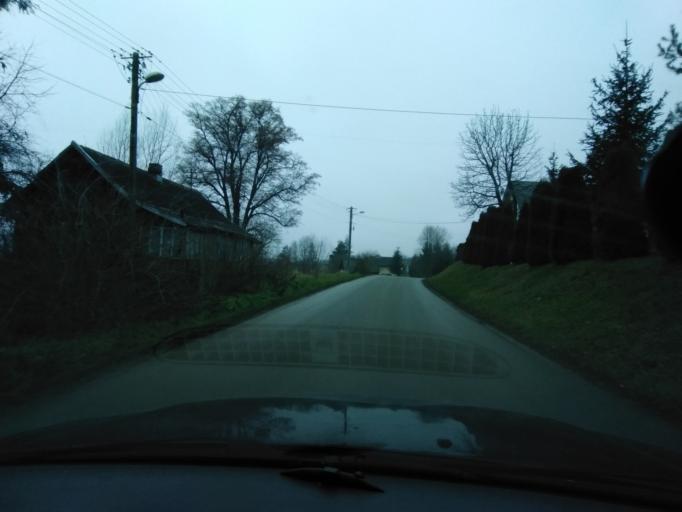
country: PL
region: Subcarpathian Voivodeship
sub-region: Powiat przeworski
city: Zarzecze
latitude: 49.9915
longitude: 22.5240
